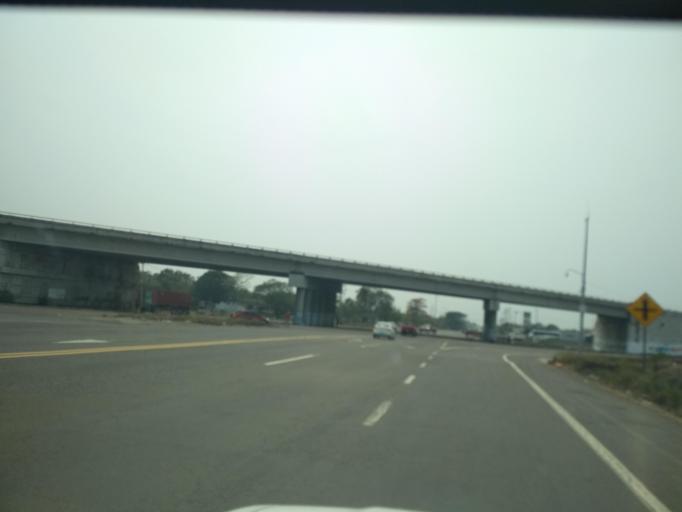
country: MX
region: Veracruz
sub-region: Veracruz
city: Delfino Victoria (Santa Fe)
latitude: 19.1885
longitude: -96.2737
